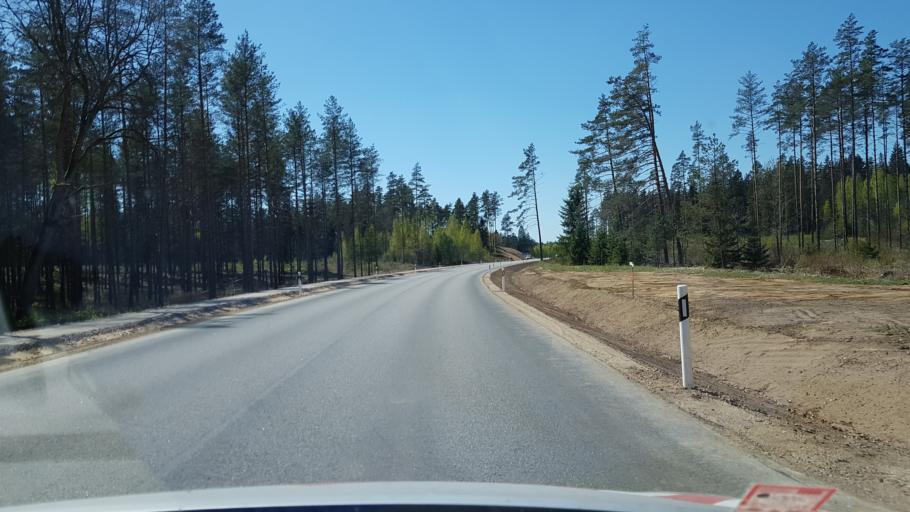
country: EE
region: Vorumaa
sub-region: Voru linn
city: Voru
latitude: 57.8748
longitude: 26.8184
